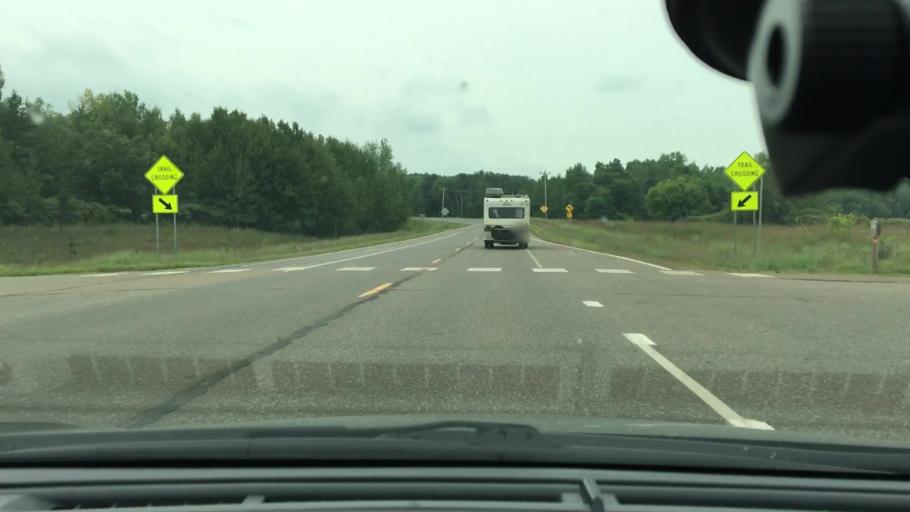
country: US
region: Minnesota
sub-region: Crow Wing County
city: Crosby
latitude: 46.4913
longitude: -93.9563
